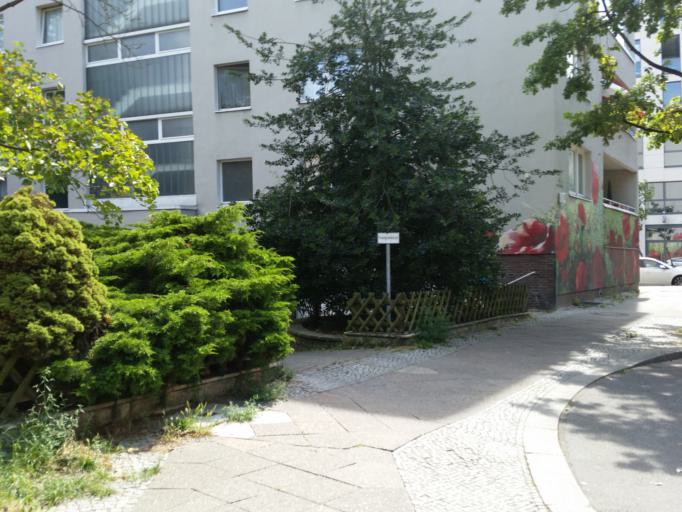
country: DE
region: Berlin
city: Berlin Schoeneberg
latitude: 52.4891
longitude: 13.3423
